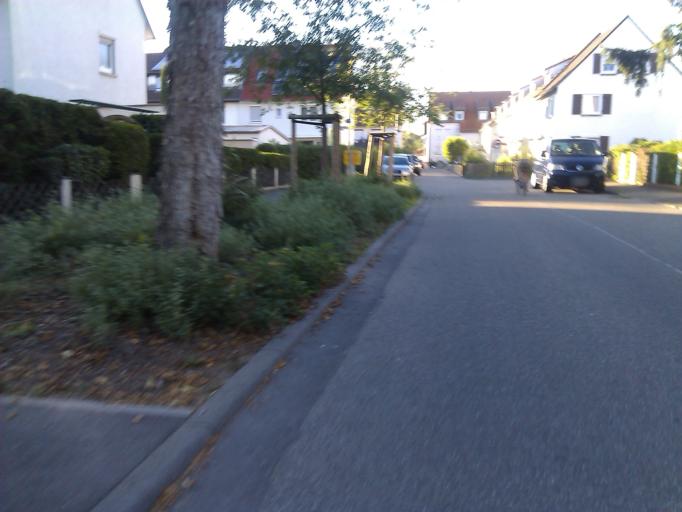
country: DE
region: Baden-Wuerttemberg
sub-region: Regierungsbezirk Stuttgart
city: Neckarsulm
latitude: 49.2012
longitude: 9.2299
